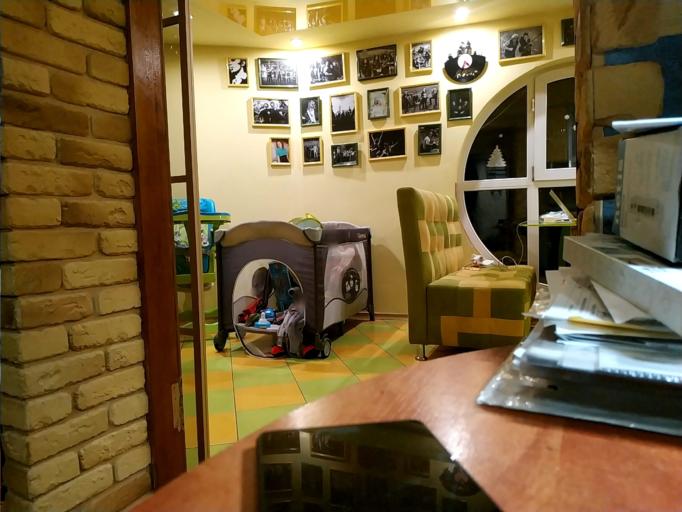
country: RU
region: Orjol
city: Naryshkino
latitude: 53.0180
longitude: 35.6904
